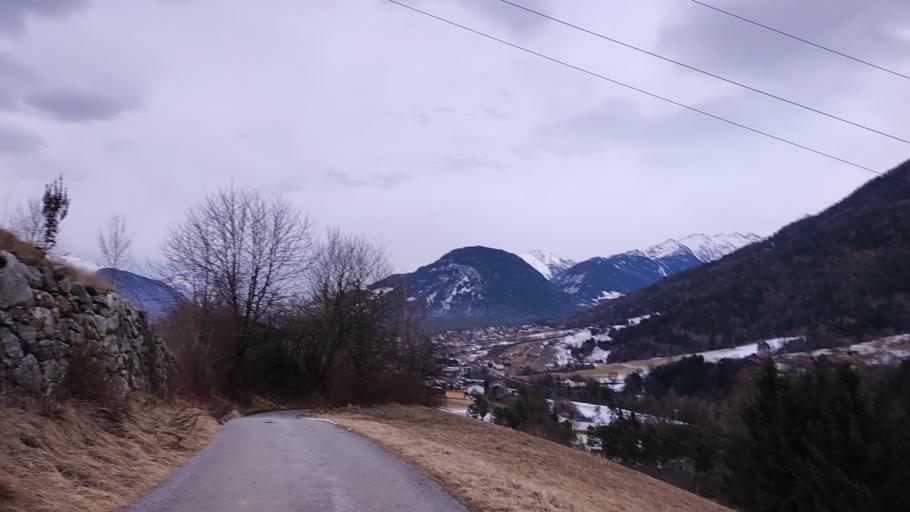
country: AT
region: Tyrol
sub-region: Politischer Bezirk Imst
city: Roppen
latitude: 47.2134
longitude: 10.8029
